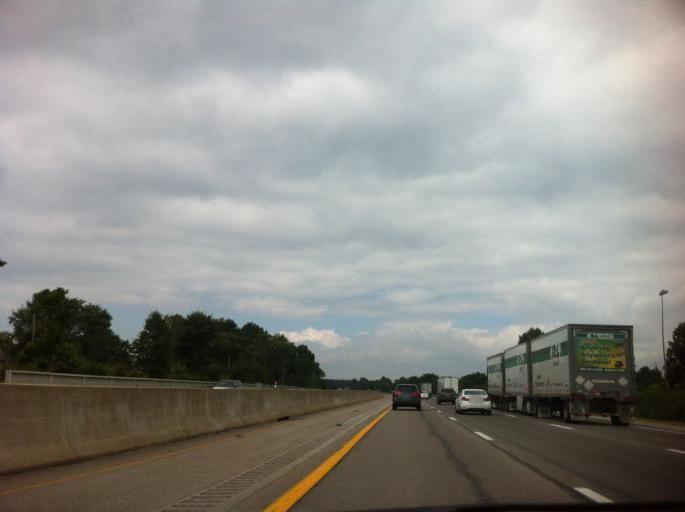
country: US
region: Ohio
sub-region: Cuyahoga County
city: Berea
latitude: 41.3524
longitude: -81.8701
